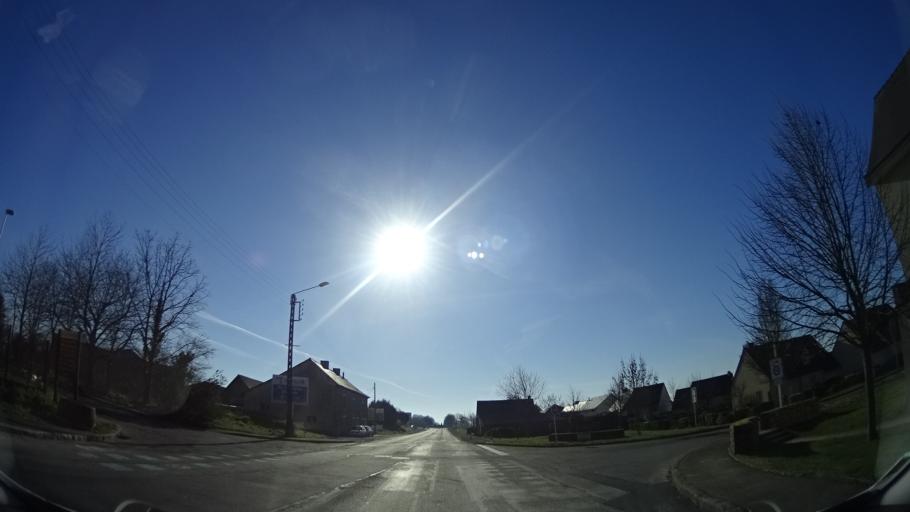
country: FR
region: Brittany
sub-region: Departement d'Ille-et-Vilaine
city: La Meziere
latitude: 48.2162
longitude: -1.7465
